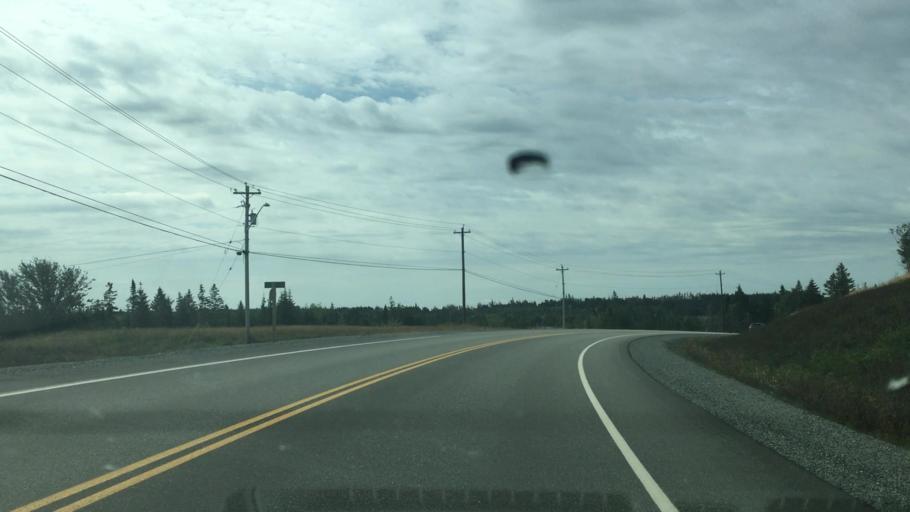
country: CA
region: Nova Scotia
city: Princeville
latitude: 45.6606
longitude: -60.8138
